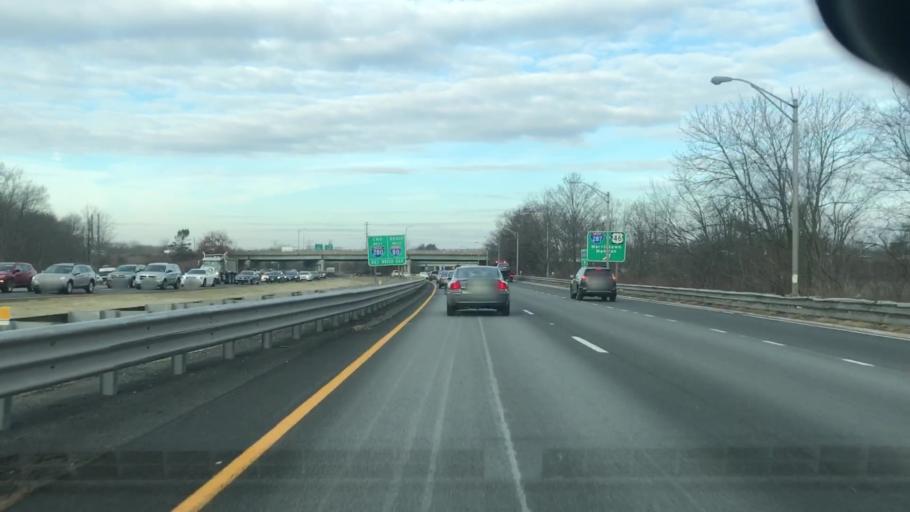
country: US
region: New Jersey
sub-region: Morris County
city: East Hanover
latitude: 40.8584
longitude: -74.3639
